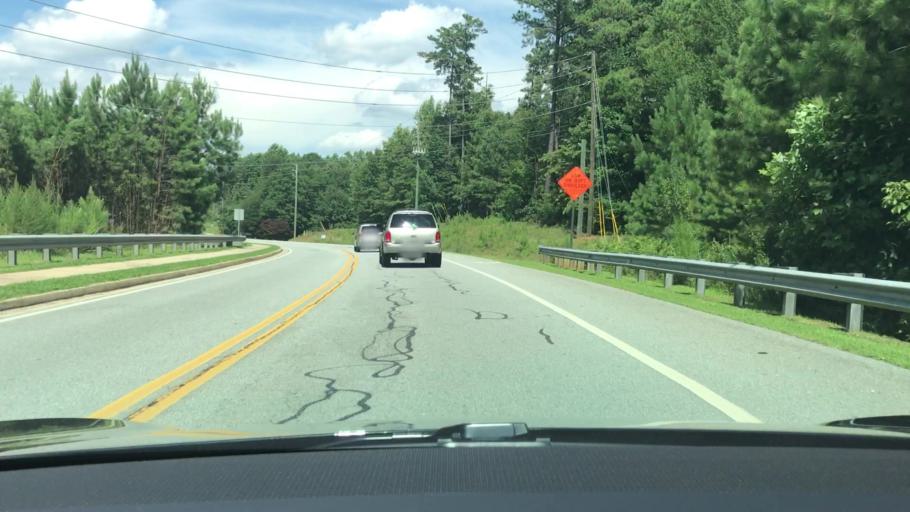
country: US
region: Georgia
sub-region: Gwinnett County
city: Sugar Hill
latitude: 34.0829
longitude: -84.0459
